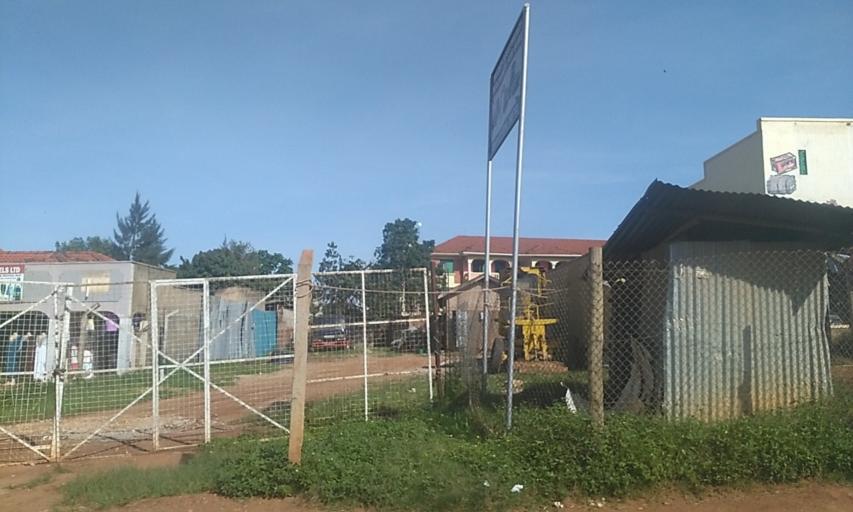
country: UG
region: Central Region
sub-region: Wakiso District
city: Kireka
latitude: 0.3721
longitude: 32.6242
